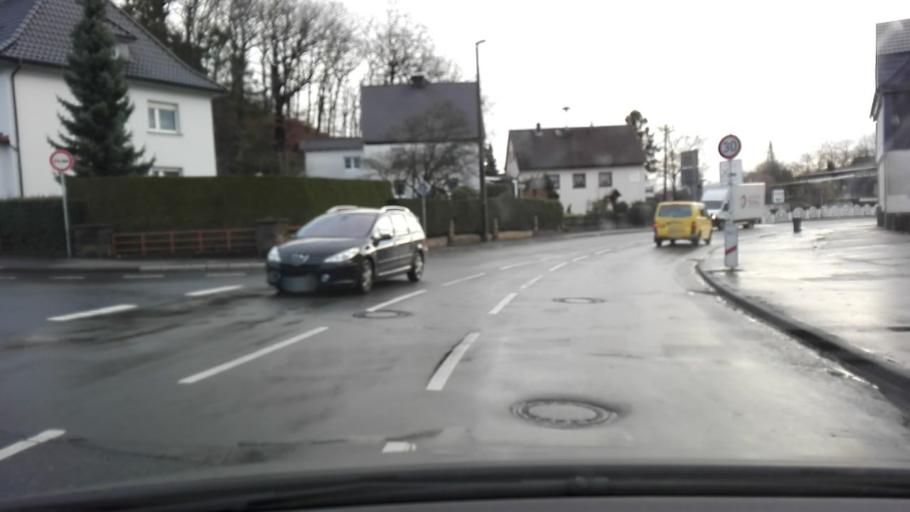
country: DE
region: North Rhine-Westphalia
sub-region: Regierungsbezirk Arnsberg
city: Frondenberg
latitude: 51.4743
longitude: 7.7776
